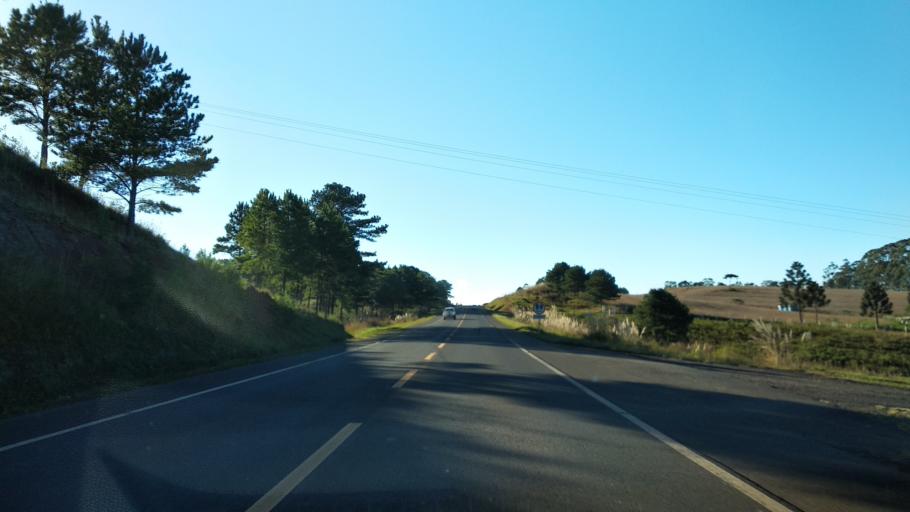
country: BR
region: Santa Catarina
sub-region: Lages
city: Lages
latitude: -27.7944
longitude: -50.4031
